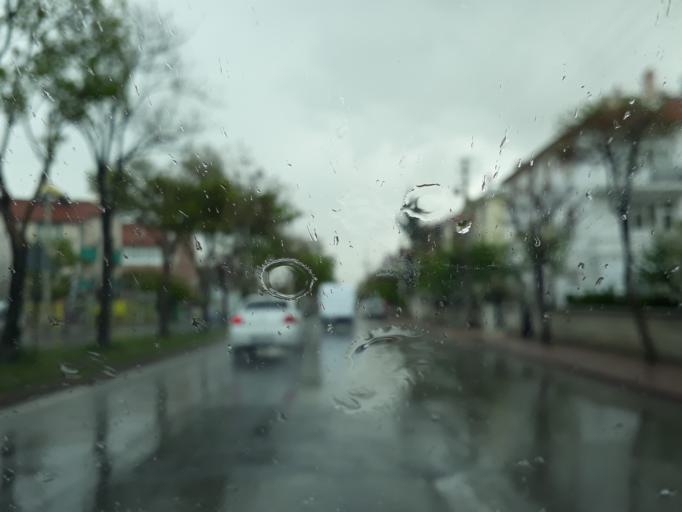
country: TR
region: Konya
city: Selcuklu
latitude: 37.9150
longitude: 32.4936
